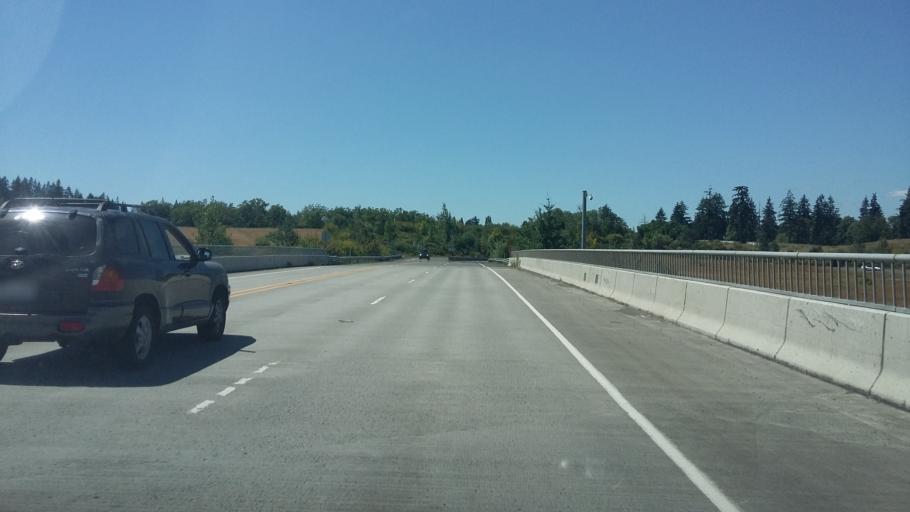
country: US
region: Washington
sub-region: Clark County
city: Mount Vista
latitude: 45.7812
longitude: -122.6733
